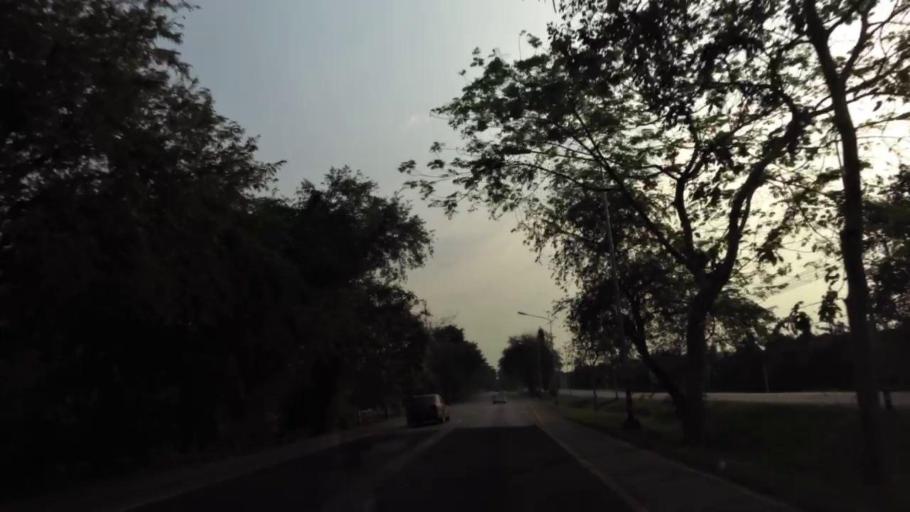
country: TH
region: Chanthaburi
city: Chanthaburi
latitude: 12.5689
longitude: 102.1622
